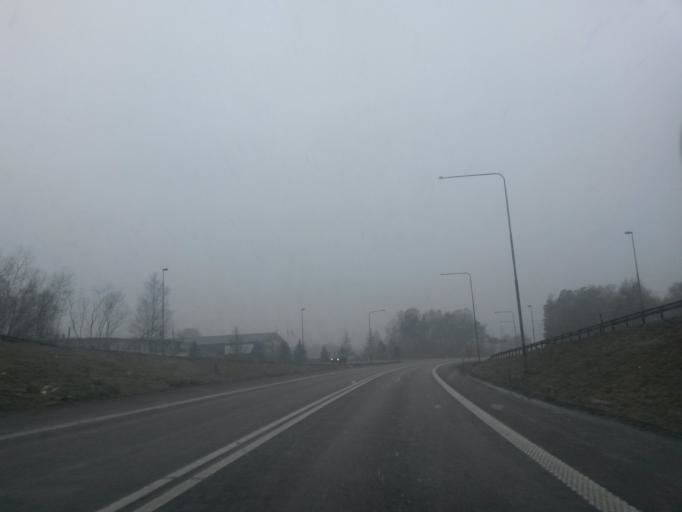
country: SE
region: Vaestra Goetaland
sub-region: Trollhattan
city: Trollhattan
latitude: 58.3002
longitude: 12.3303
